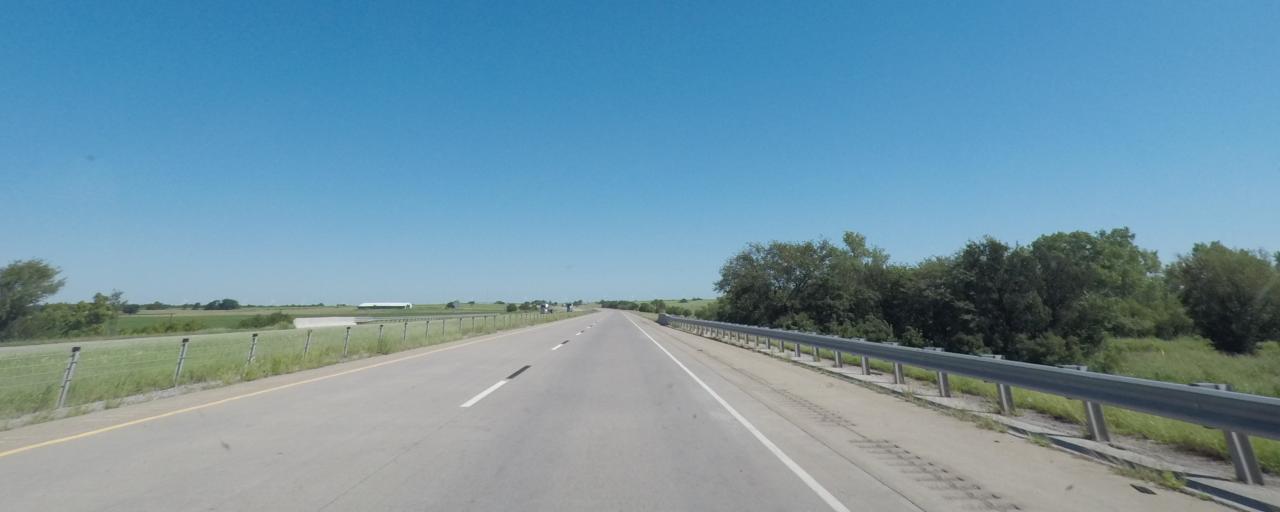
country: US
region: Oklahoma
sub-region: Noble County
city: Perry
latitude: 36.4773
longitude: -97.3269
